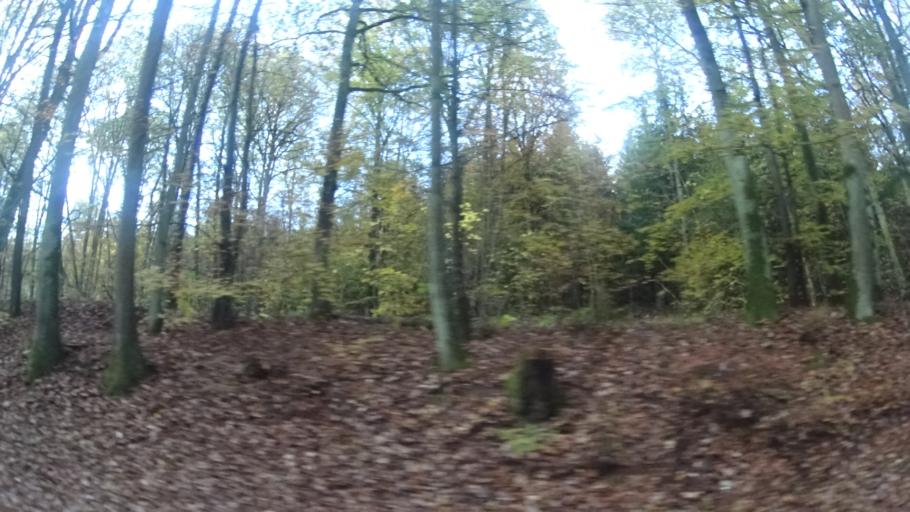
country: DE
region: Thuringia
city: Dingsleben
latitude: 50.4051
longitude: 10.6014
